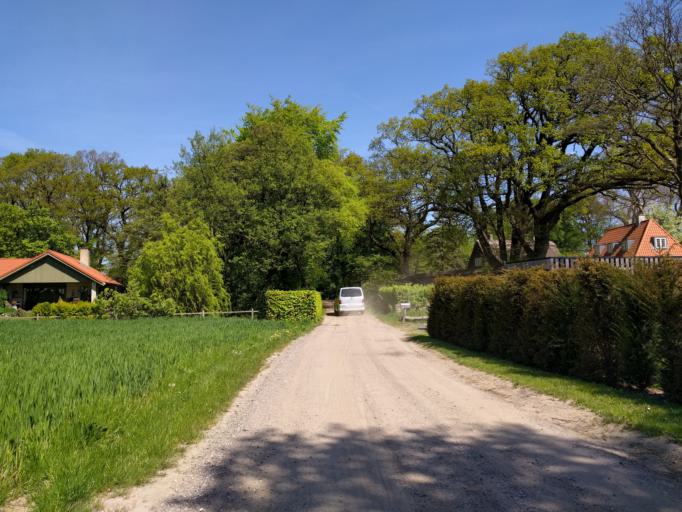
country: DK
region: Zealand
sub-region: Guldborgsund Kommune
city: Stubbekobing
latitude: 54.7549
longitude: 12.0372
